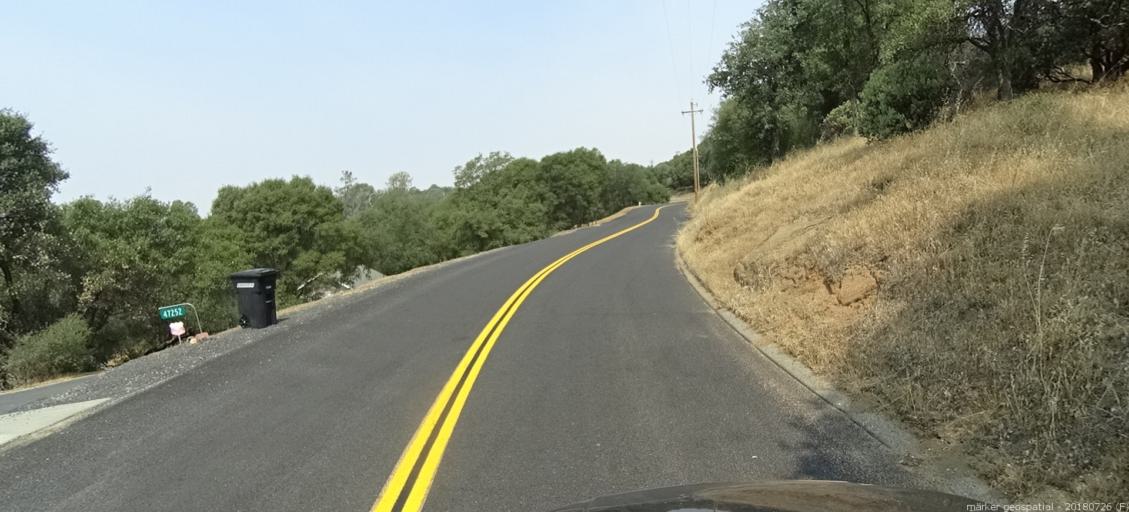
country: US
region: California
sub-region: Madera County
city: Coarsegold
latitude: 37.2494
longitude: -119.6864
